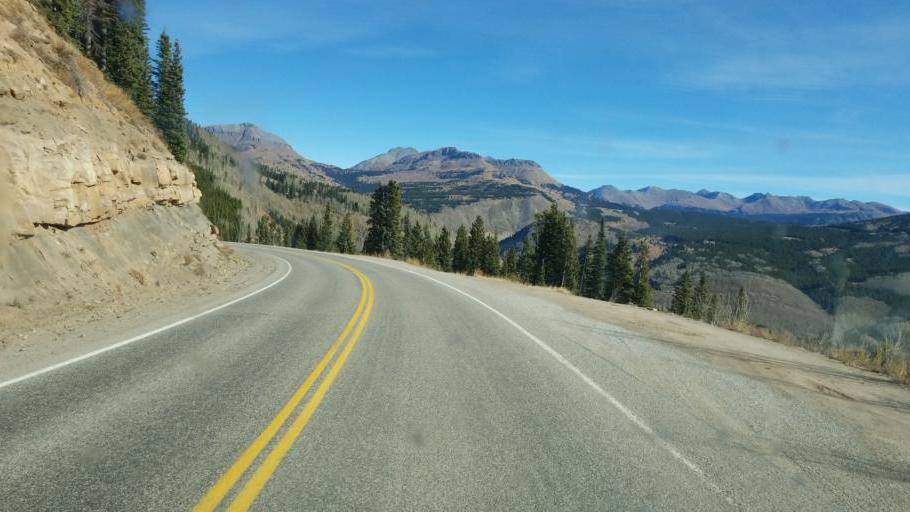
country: US
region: Colorado
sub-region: San Juan County
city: Silverton
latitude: 37.7016
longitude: -107.7687
